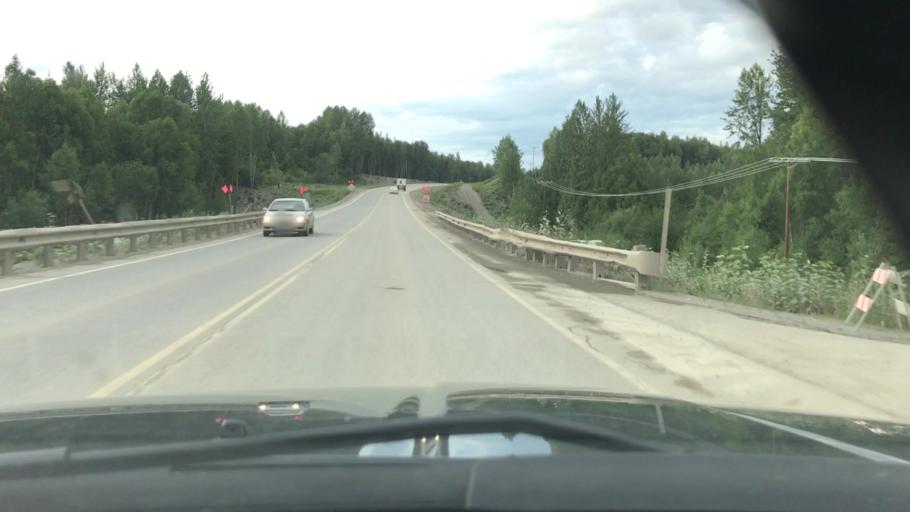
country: US
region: Alaska
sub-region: Matanuska-Susitna Borough
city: Y
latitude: 62.1050
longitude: -150.0598
